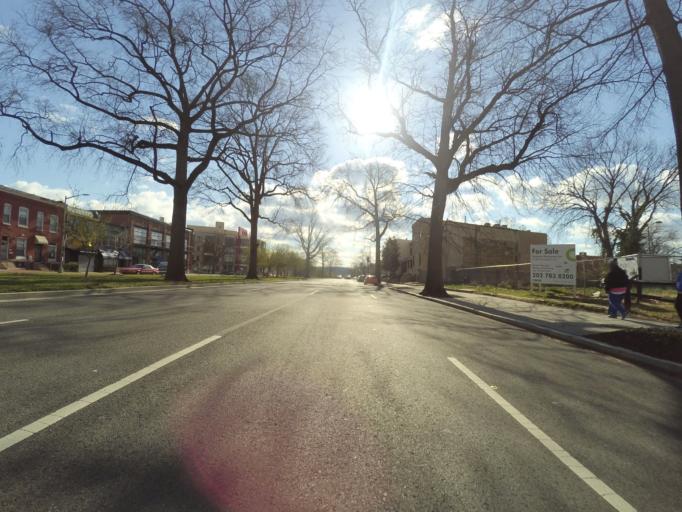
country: US
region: Maryland
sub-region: Prince George's County
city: Hillcrest Heights
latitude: 38.8799
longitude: -76.9849
